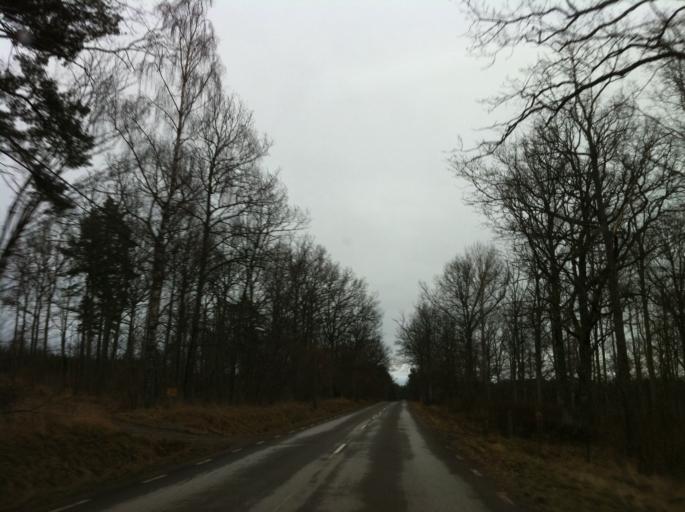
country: SE
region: Kalmar
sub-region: Vasterviks Kommun
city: Vaestervik
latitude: 57.8098
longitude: 16.5883
